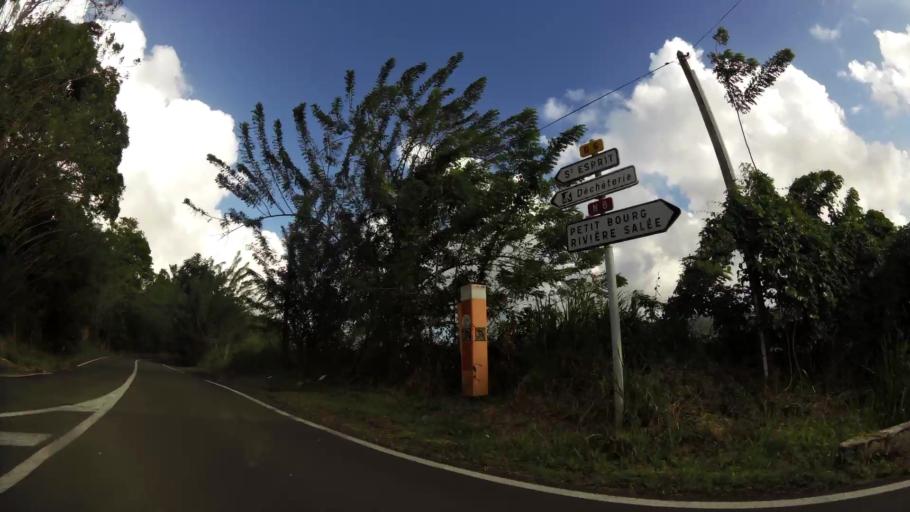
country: MQ
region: Martinique
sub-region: Martinique
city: Ducos
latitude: 14.5532
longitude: -60.9607
